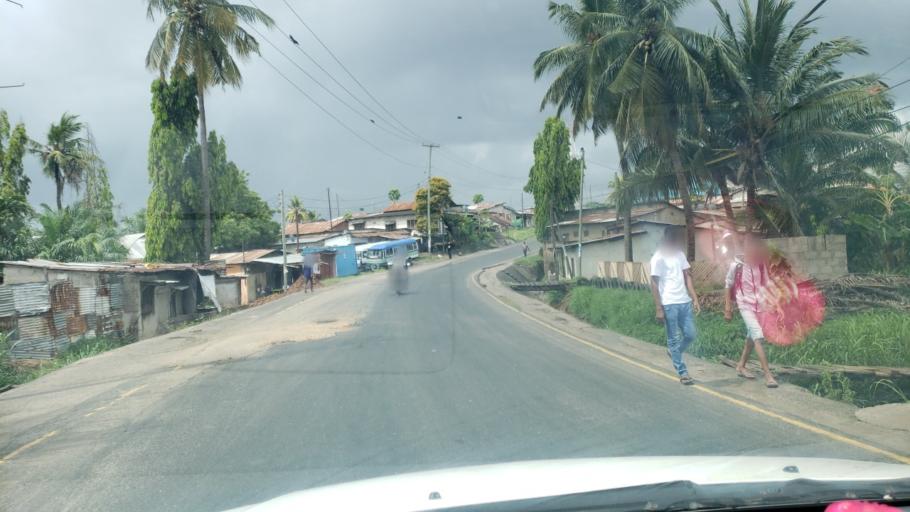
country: TZ
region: Dar es Salaam
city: Magomeni
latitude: -6.8054
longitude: 39.2448
